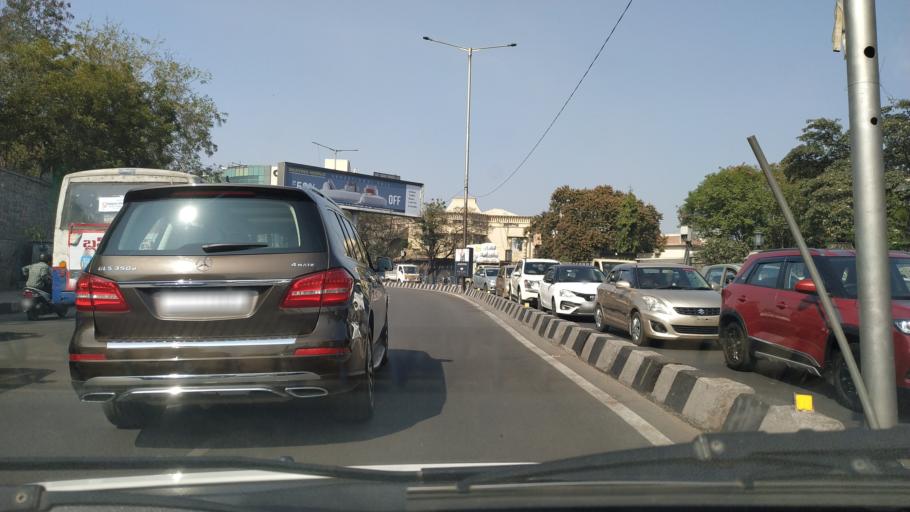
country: IN
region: Telangana
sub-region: Hyderabad
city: Hyderabad
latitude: 17.4175
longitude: 78.4490
